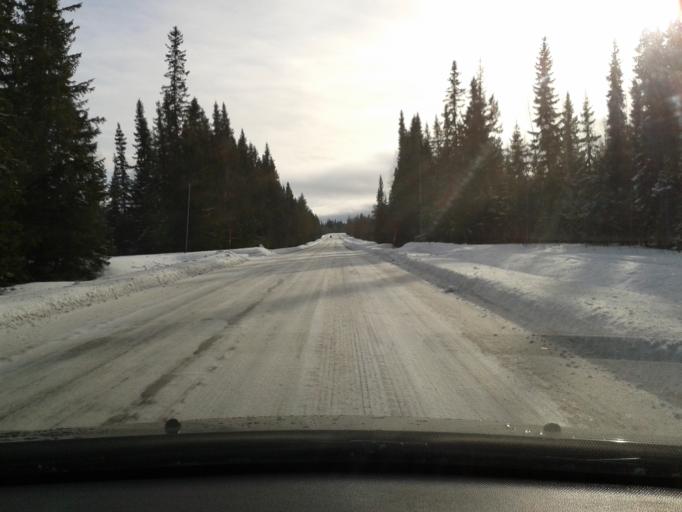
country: SE
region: Vaesterbotten
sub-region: Vilhelmina Kommun
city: Sjoberg
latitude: 64.7337
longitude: 16.2176
